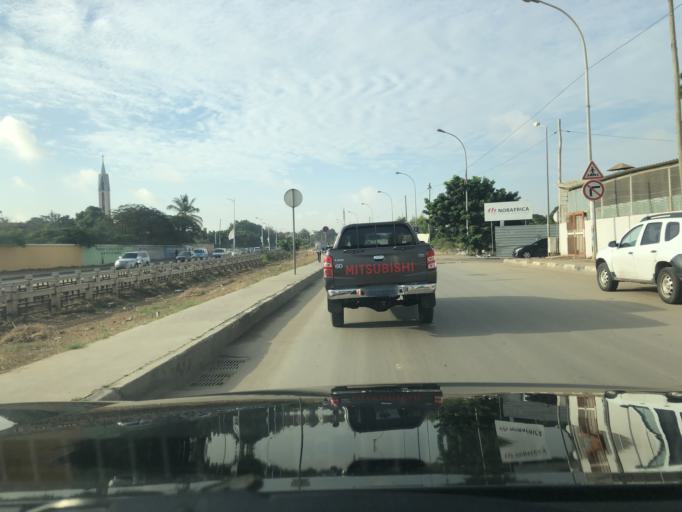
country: AO
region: Luanda
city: Luanda
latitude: -8.8292
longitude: 13.2546
